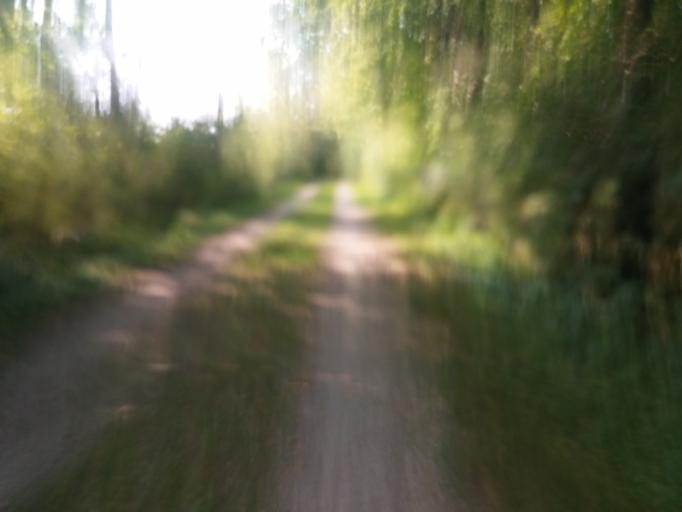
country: DE
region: Baden-Wuerttemberg
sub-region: Tuebingen Region
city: Aitrach
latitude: 47.9500
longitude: 10.0884
